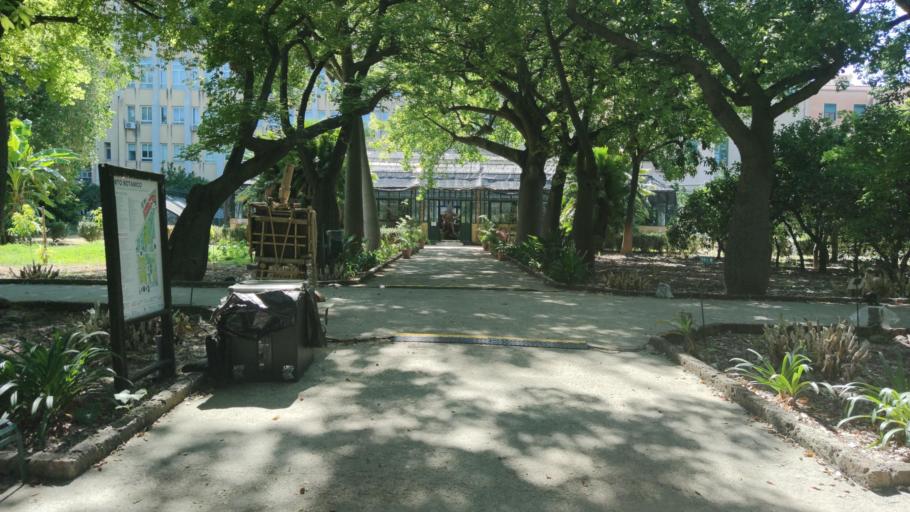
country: IT
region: Sicily
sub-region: Palermo
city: Palermo
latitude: 38.1123
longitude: 13.3729
